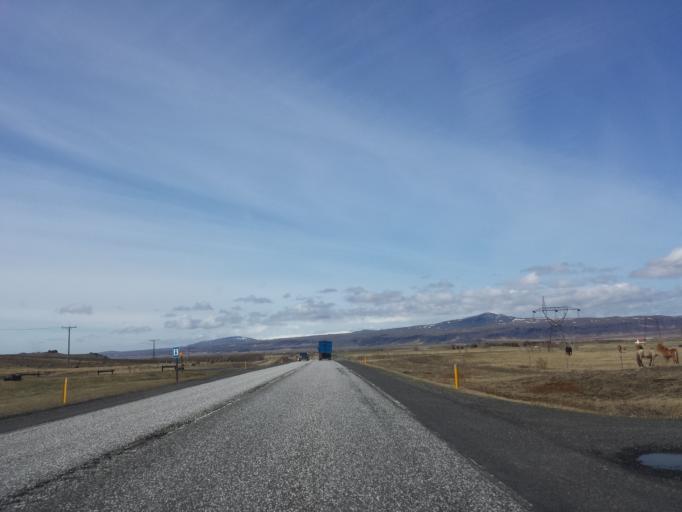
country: IS
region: South
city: Selfoss
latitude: 63.9580
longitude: -21.0777
